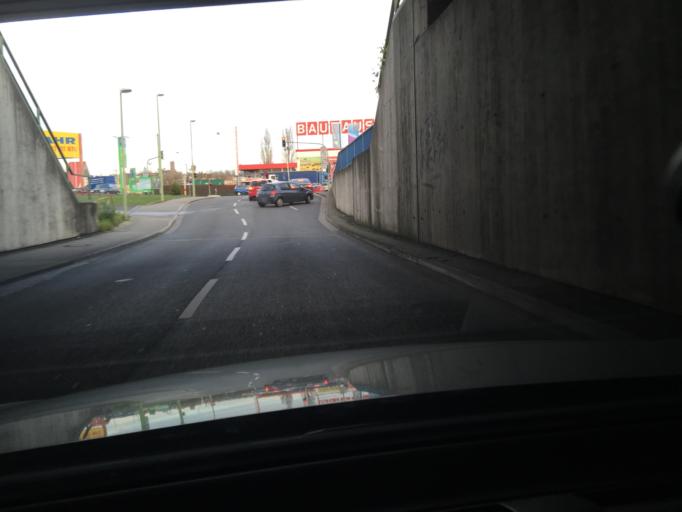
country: DE
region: North Rhine-Westphalia
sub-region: Regierungsbezirk Arnsberg
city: Hagen
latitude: 51.3745
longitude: 7.4547
